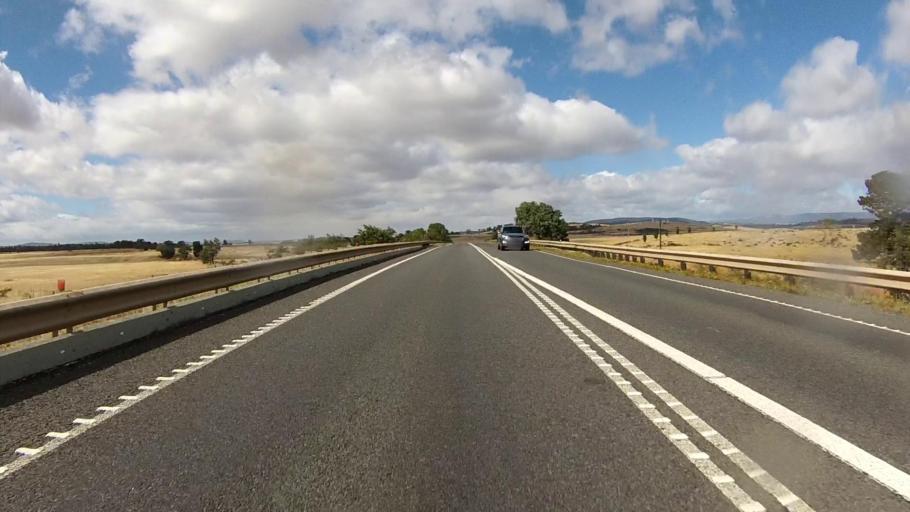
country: AU
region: Tasmania
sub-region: Northern Midlands
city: Evandale
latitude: -41.8387
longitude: 147.4482
